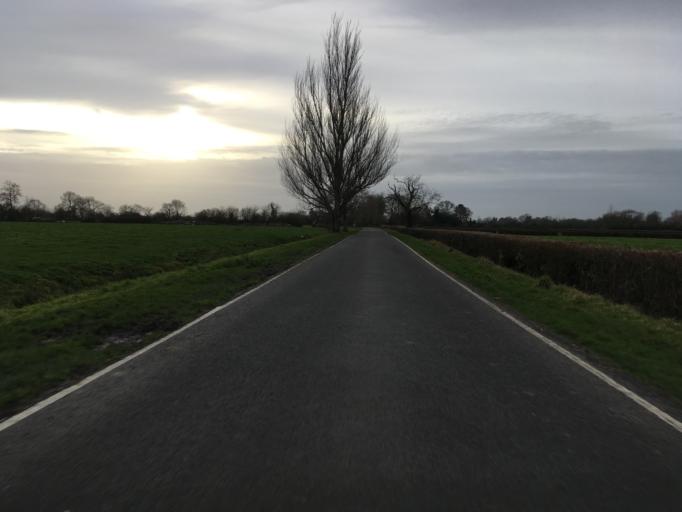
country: GB
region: Wales
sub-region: Newport
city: Redwick
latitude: 51.5573
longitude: -2.8361
